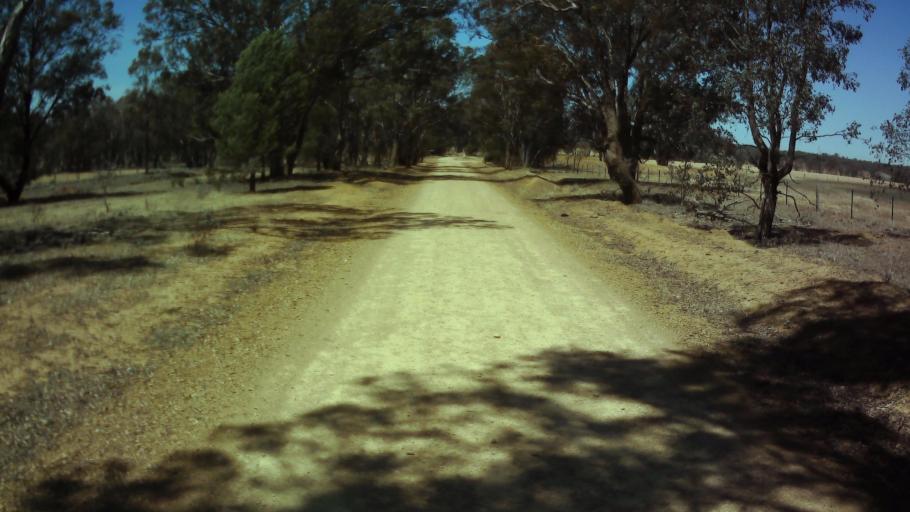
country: AU
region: New South Wales
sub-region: Weddin
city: Grenfell
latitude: -33.9207
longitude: 148.2040
